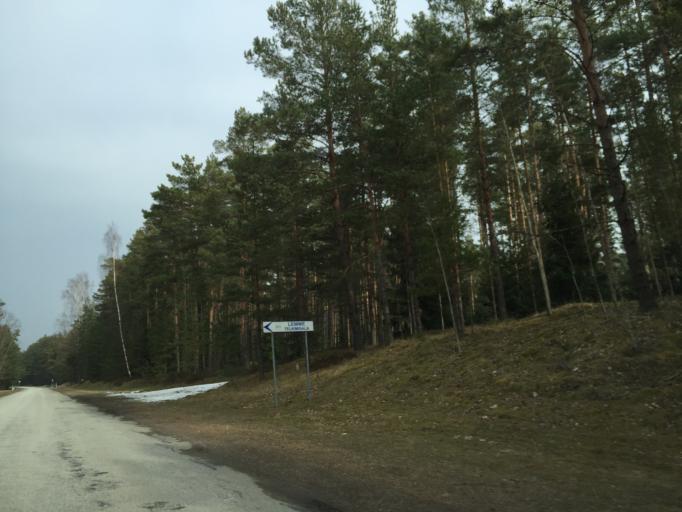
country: LV
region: Salacgrivas
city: Ainazi
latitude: 57.9648
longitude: 24.4067
